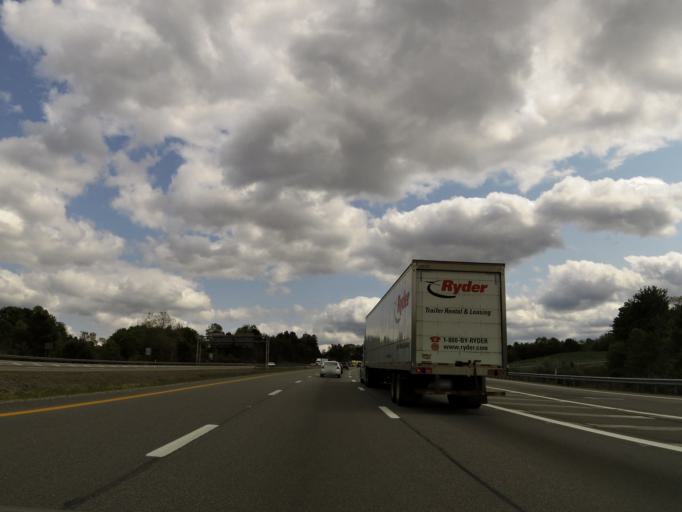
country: US
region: West Virginia
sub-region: Raleigh County
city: Prosperity
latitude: 37.8339
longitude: -81.2146
